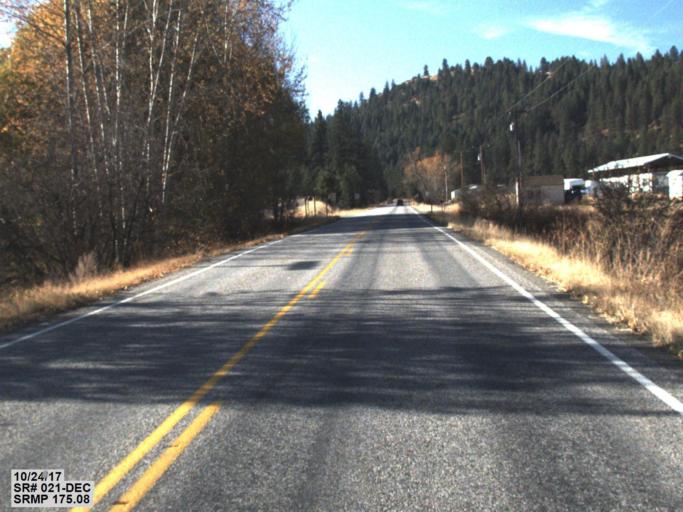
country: US
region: Washington
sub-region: Ferry County
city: Republic
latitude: 48.8013
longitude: -118.6088
